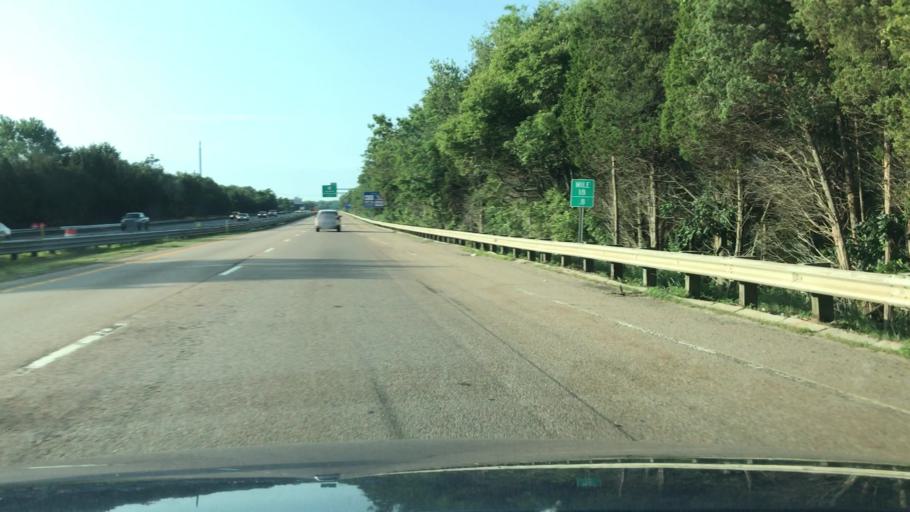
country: US
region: Massachusetts
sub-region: Plymouth County
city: Kingston
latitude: 42.0021
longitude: -70.7237
